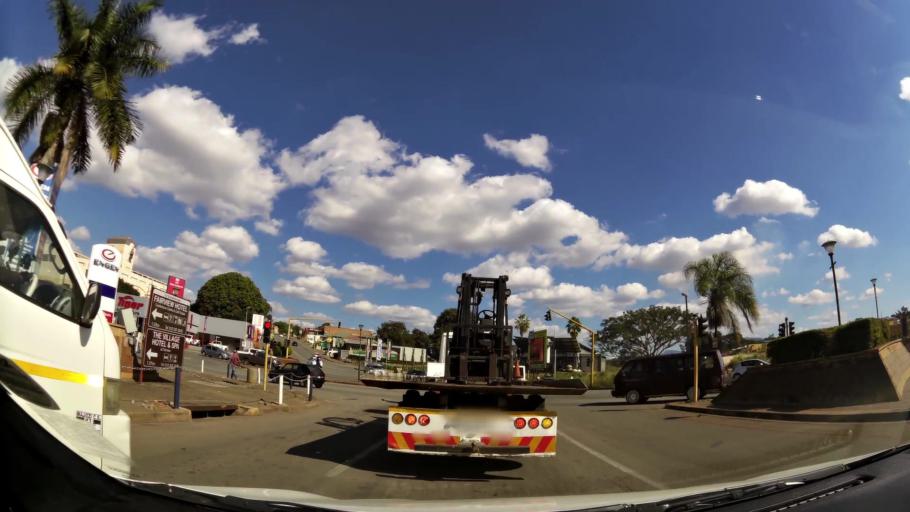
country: ZA
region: Limpopo
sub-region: Mopani District Municipality
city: Tzaneen
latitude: -23.8242
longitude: 30.1592
